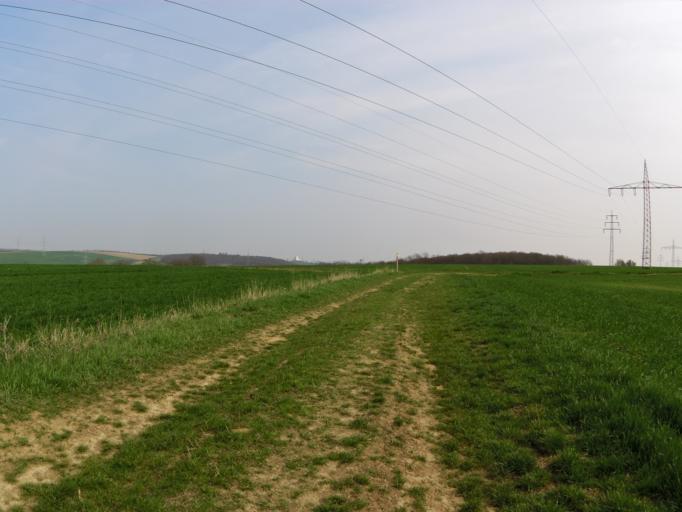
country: DE
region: Bavaria
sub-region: Regierungsbezirk Unterfranken
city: Rottendorf
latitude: 49.7784
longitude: 10.0310
